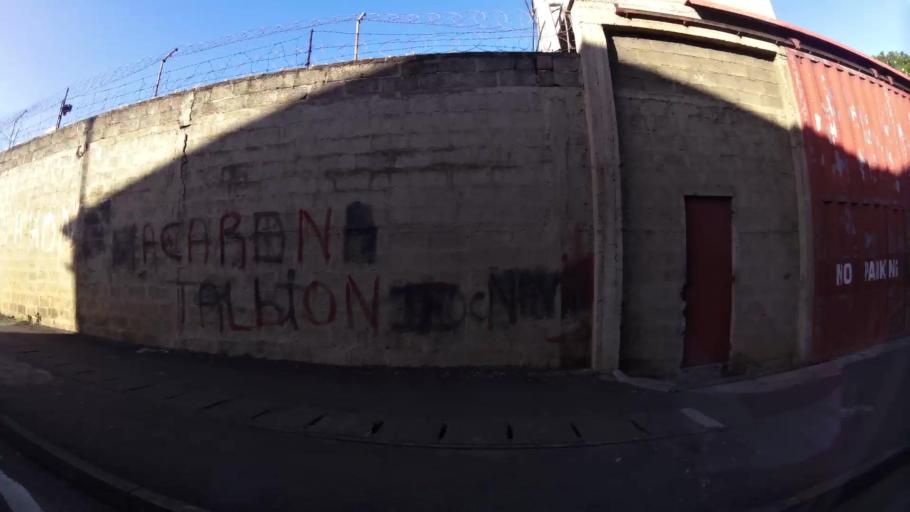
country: MU
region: Port Louis
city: Port Louis
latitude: -20.1556
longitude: 57.5059
